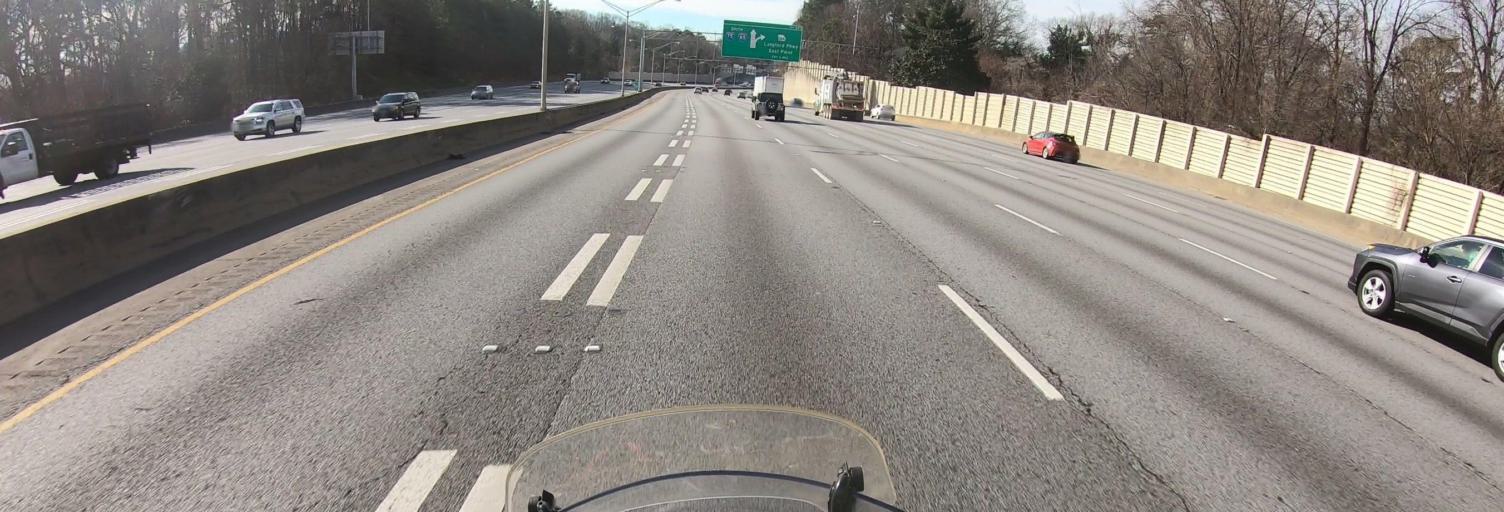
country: US
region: Georgia
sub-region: Fulton County
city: Atlanta
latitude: 33.7153
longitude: -84.3971
